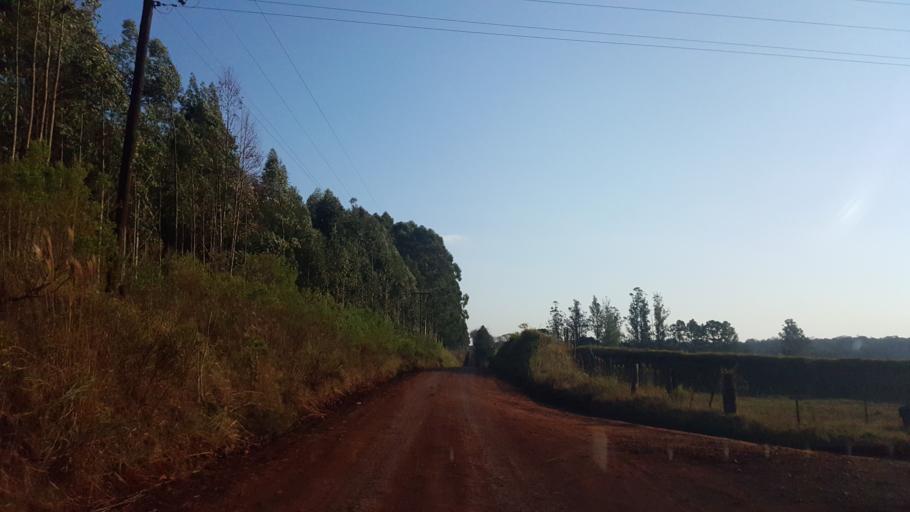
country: AR
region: Misiones
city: Capiovi
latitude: -26.9167
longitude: -55.0515
